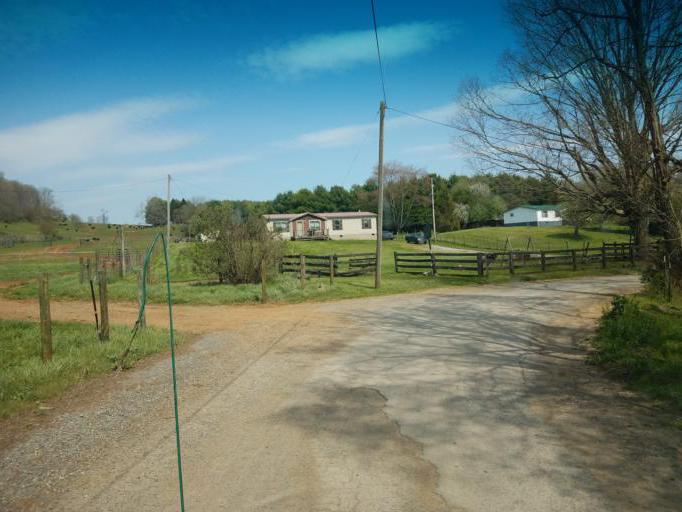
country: US
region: Virginia
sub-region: Smyth County
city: Marion
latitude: 36.7749
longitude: -81.4534
